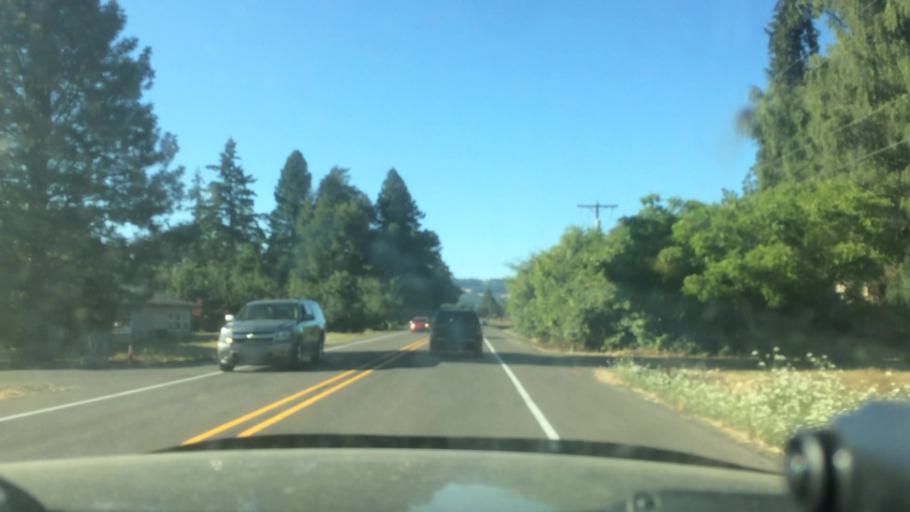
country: US
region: Oregon
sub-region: Yamhill County
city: Newberg
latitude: 45.2809
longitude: -122.9448
